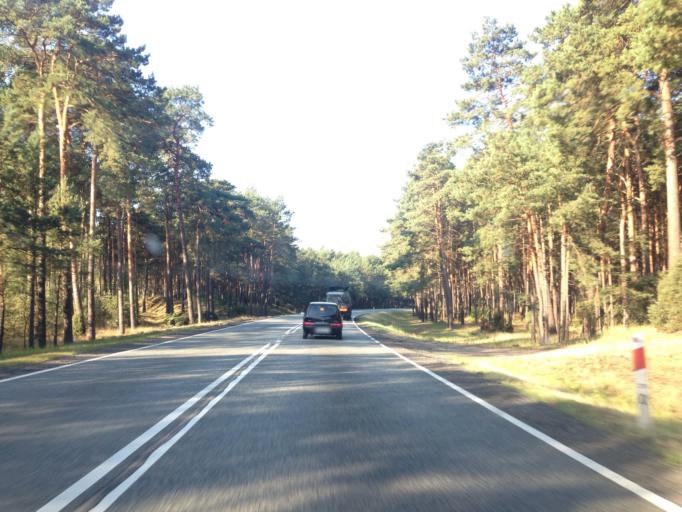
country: PL
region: Kujawsko-Pomorskie
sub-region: Powiat bydgoski
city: Nowa Wies Wielka
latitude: 53.0550
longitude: 18.0634
